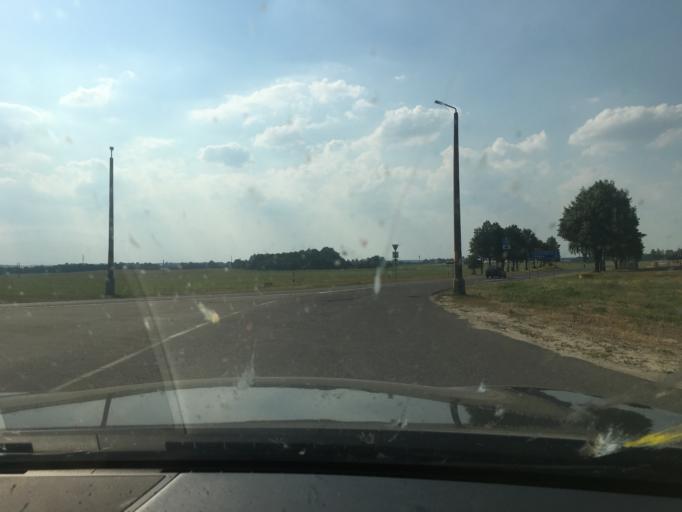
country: BY
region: Grodnenskaya
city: Svislach
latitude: 53.0429
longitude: 24.0859
